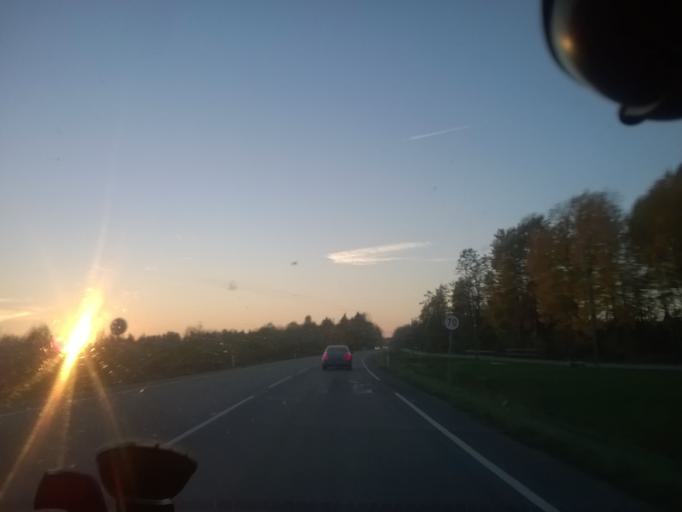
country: EE
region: Laeaene
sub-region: Ridala Parish
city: Uuemoisa
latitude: 58.9556
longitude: 23.7559
